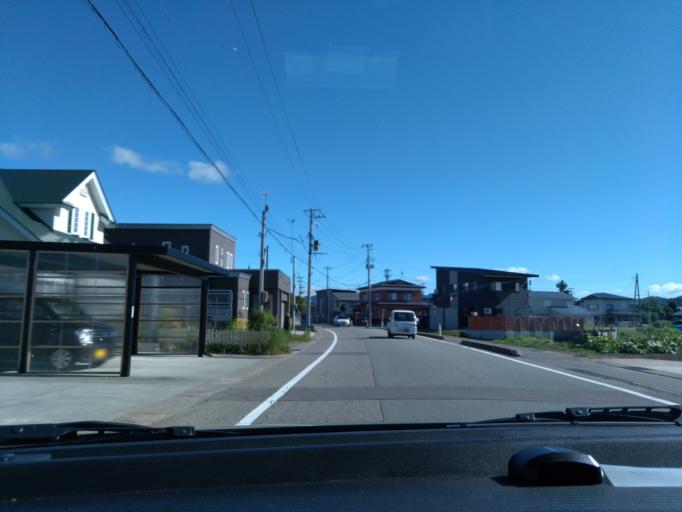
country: JP
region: Akita
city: Yuzawa
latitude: 39.2038
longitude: 140.5513
